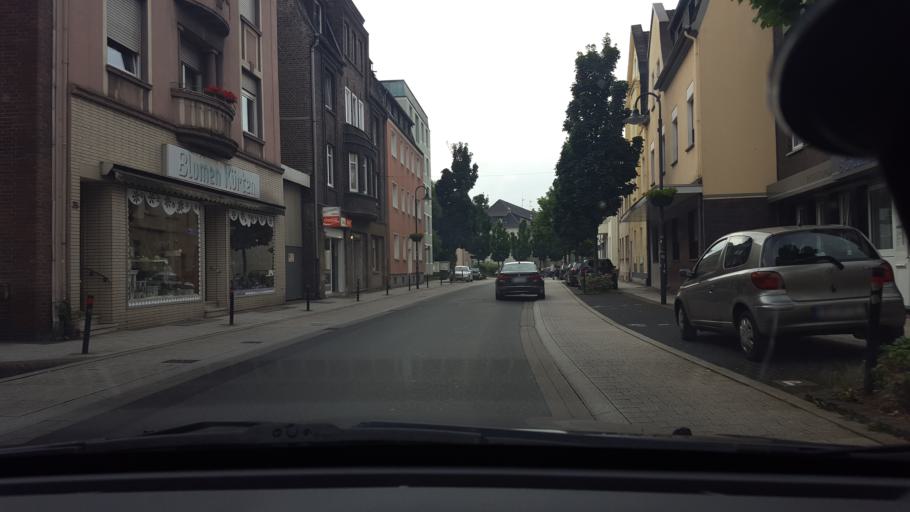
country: DE
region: North Rhine-Westphalia
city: Herten
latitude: 51.6012
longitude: 7.0888
